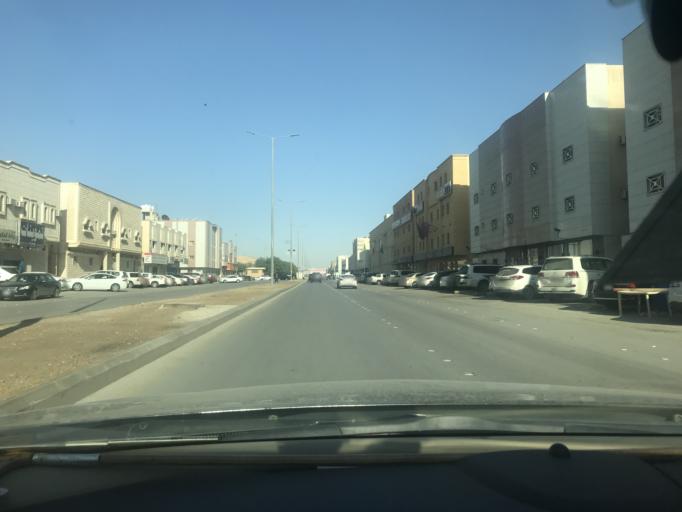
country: SA
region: Ar Riyad
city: Riyadh
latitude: 24.7520
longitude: 46.6700
